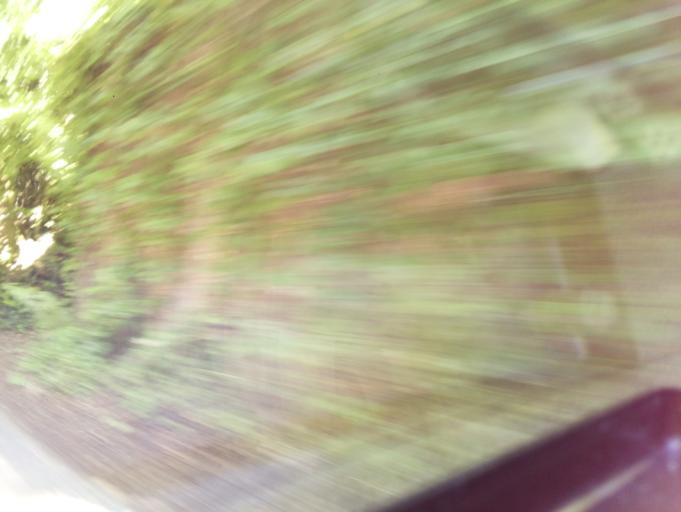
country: GB
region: Wales
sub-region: Monmouthshire
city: Tintern
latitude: 51.6984
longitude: -2.7138
